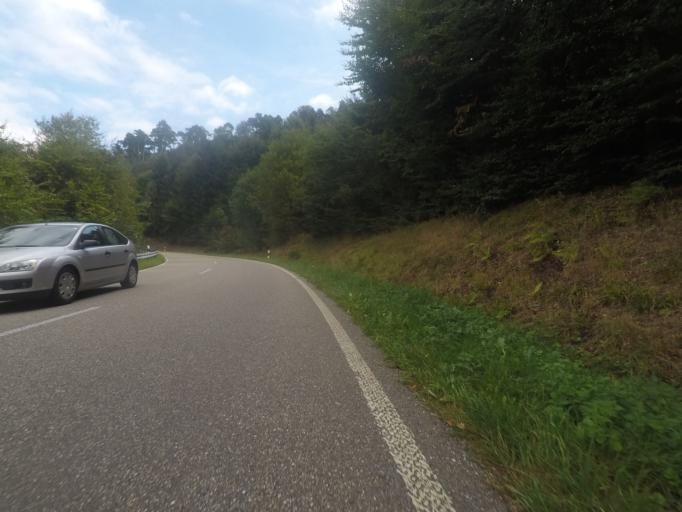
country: DE
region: Baden-Wuerttemberg
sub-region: Karlsruhe Region
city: Gaggenau
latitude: 48.8340
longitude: 8.3717
